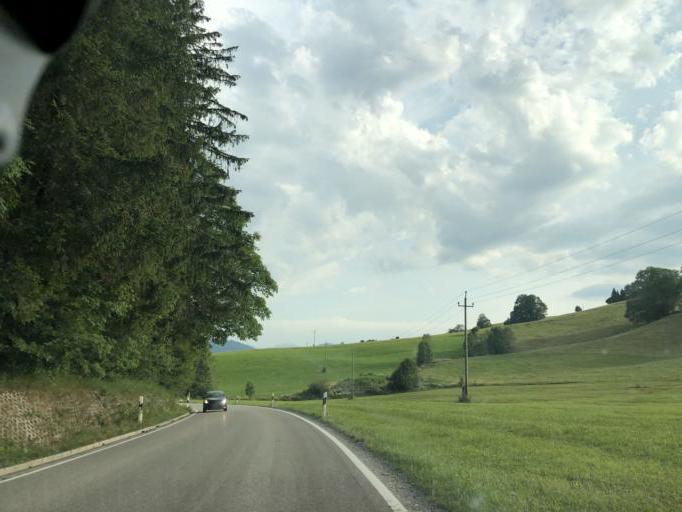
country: DE
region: Bavaria
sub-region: Swabia
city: Gorisried
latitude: 47.6780
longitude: 10.4711
